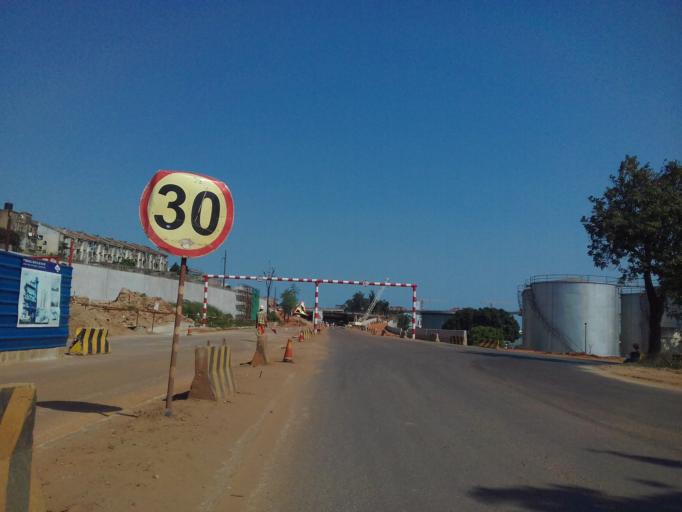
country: MZ
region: Maputo City
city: Maputo
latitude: -25.9574
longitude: 32.5541
